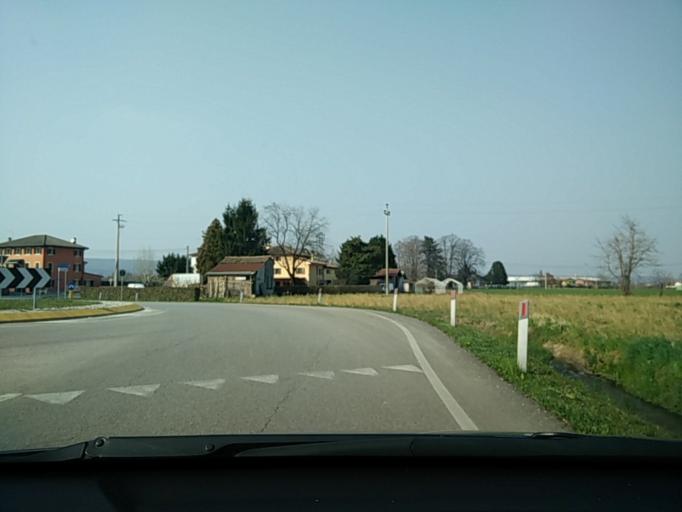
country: IT
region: Veneto
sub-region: Provincia di Treviso
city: Camalo
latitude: 45.7628
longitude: 12.1569
